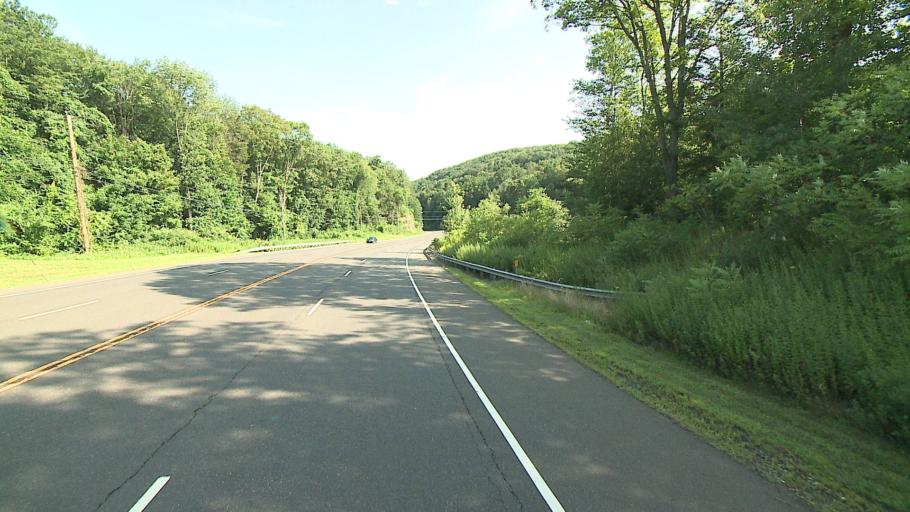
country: US
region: Connecticut
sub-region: Fairfield County
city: Danbury
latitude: 41.3504
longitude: -73.4695
